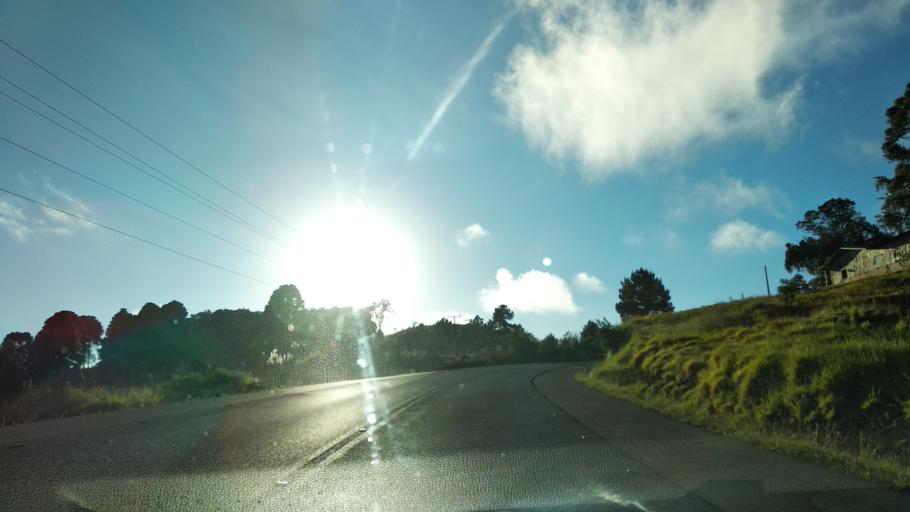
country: BR
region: Santa Catarina
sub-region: Correia Pinto
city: Correia Pinto
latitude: -27.6135
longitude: -50.6956
